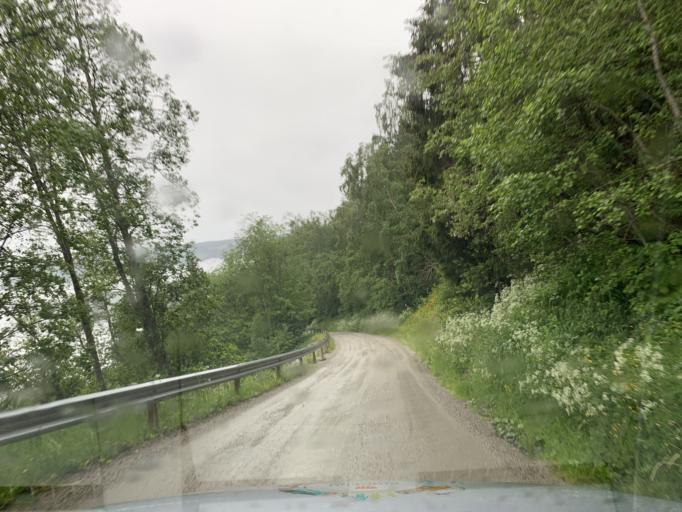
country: NO
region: Oppland
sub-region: Oyer
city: Tretten
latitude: 61.3916
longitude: 10.2720
